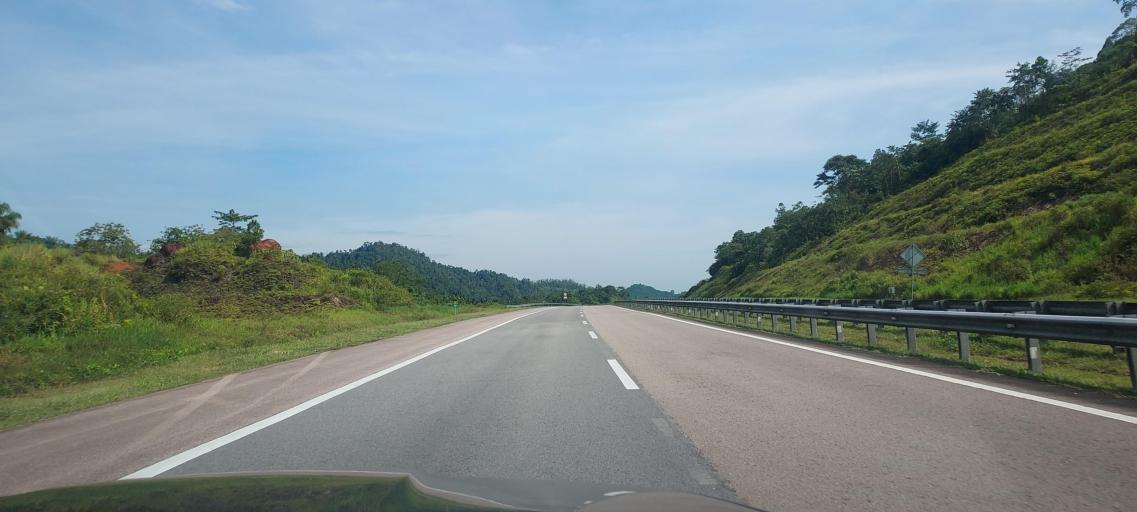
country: MY
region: Terengganu
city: Marang
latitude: 4.9470
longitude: 103.0906
